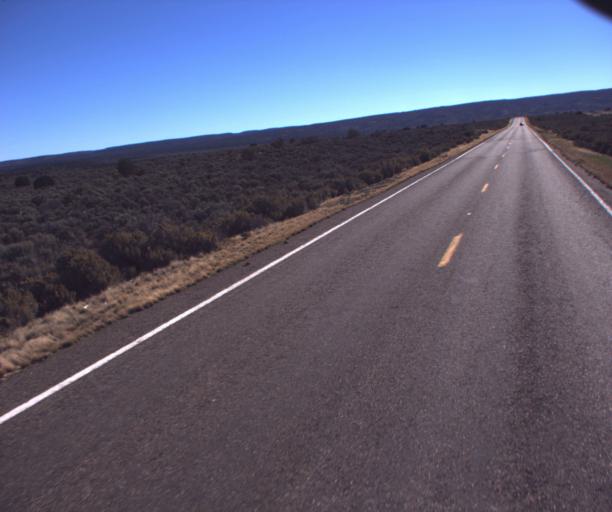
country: US
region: Arizona
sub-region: Coconino County
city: Fredonia
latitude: 36.8642
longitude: -112.3157
